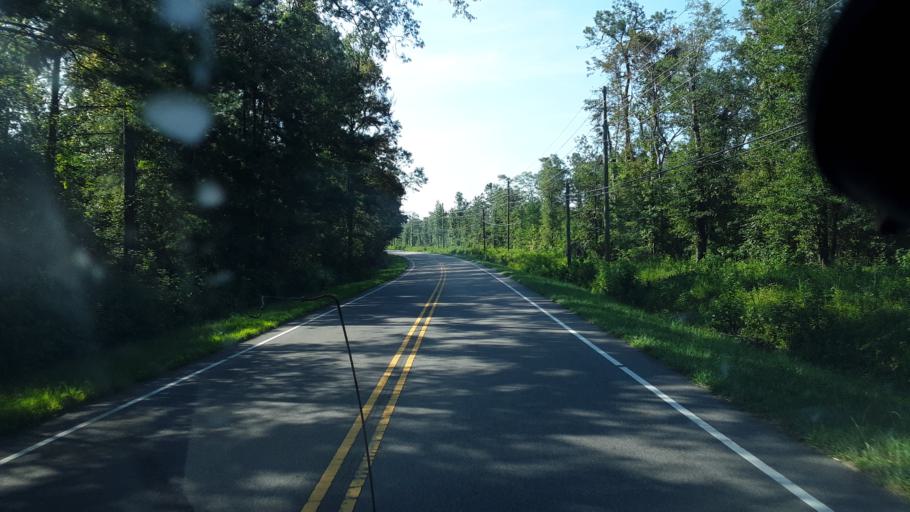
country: US
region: North Carolina
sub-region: Brunswick County
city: Belville
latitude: 34.1698
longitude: -77.9898
